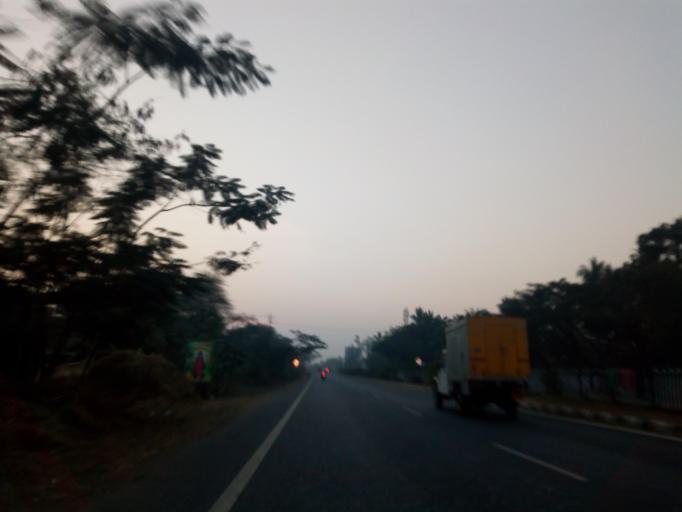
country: IN
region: Andhra Pradesh
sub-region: West Godavari
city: Tadepallegudem
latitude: 16.8236
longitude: 81.4251
